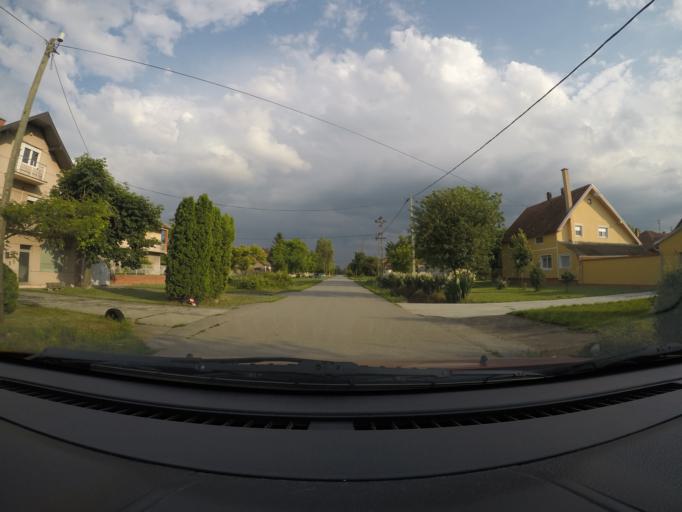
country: RS
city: Debeljaca
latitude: 45.0740
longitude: 20.5999
